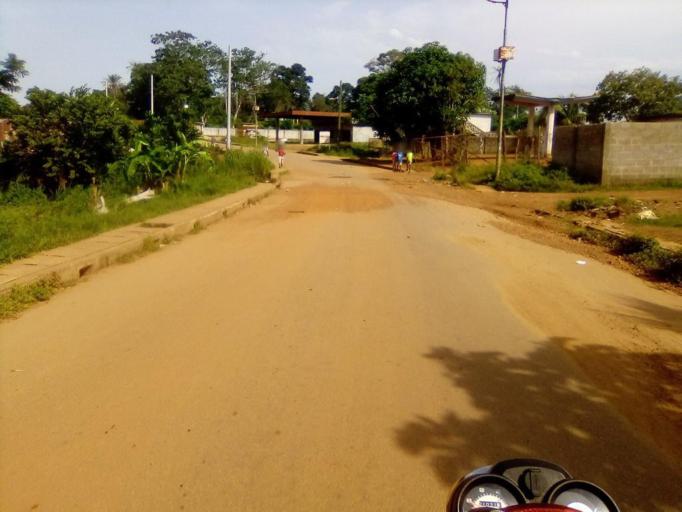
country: SL
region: Southern Province
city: Pujehun
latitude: 7.3597
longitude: -11.7261
